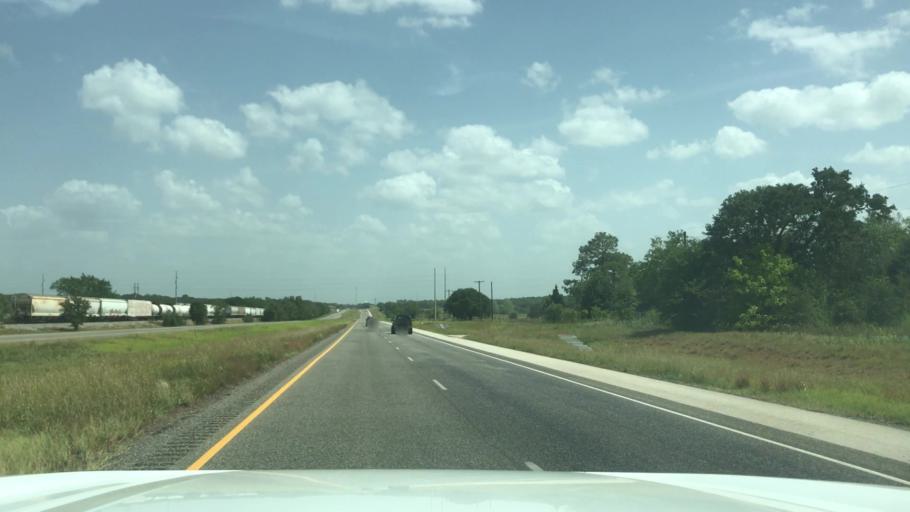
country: US
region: Texas
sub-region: Robertson County
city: Hearne
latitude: 30.9204
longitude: -96.6227
